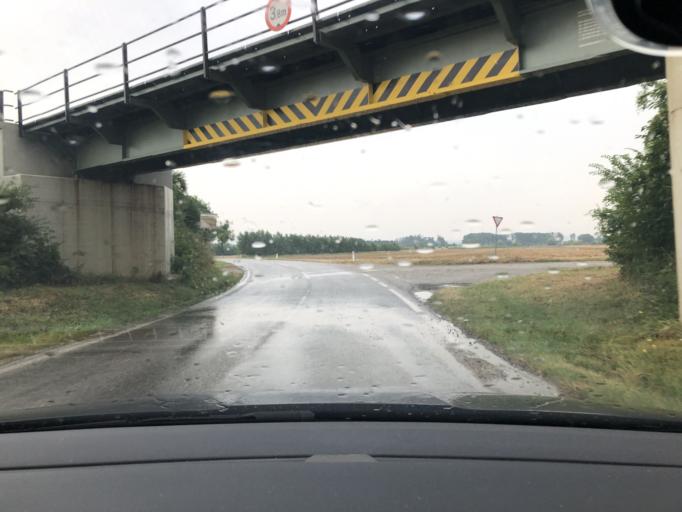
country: AT
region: Lower Austria
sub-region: Politischer Bezirk Ganserndorf
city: Weikendorf
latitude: 48.3354
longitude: 16.7787
